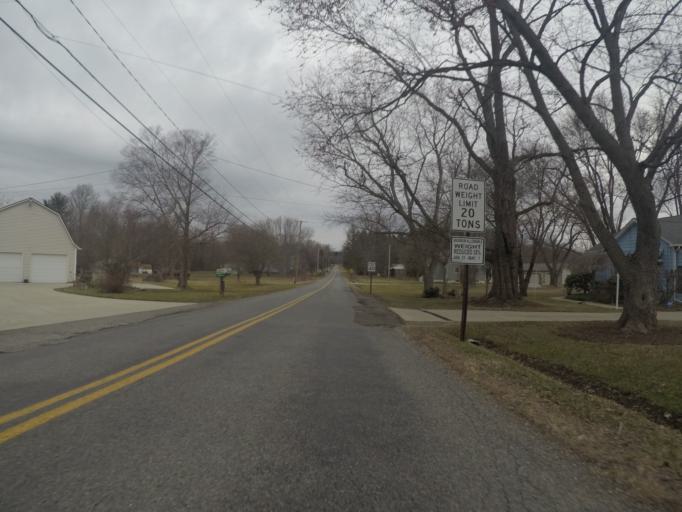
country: US
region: Ohio
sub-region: Portage County
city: Ravenna
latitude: 41.1653
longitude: -81.2808
